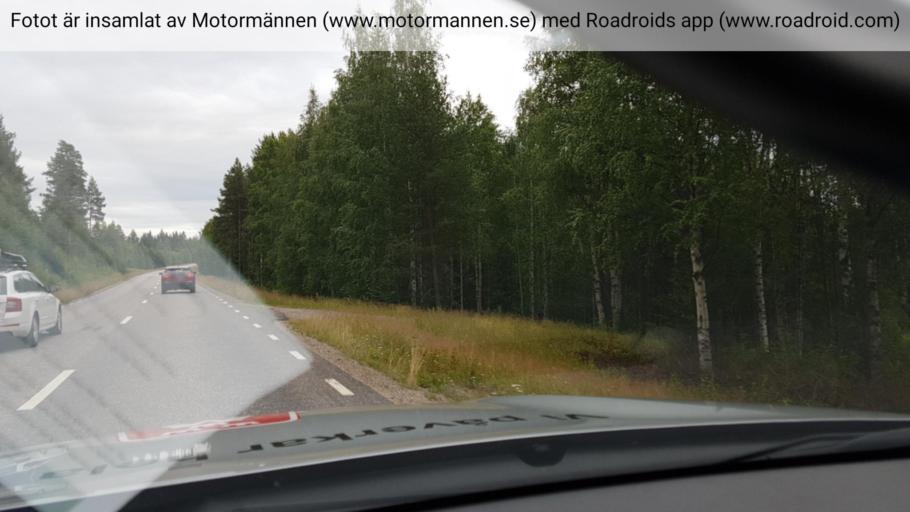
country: SE
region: Norrbotten
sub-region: Overkalix Kommun
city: OEverkalix
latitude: 66.5368
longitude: 22.7550
